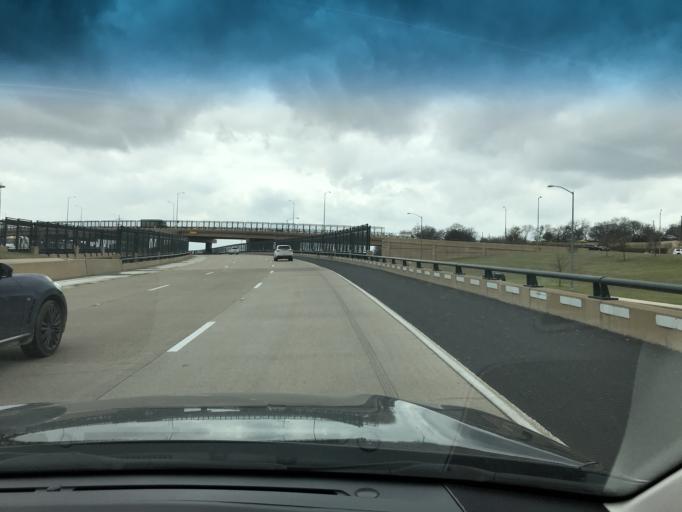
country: US
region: Texas
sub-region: Tarrant County
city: Westworth
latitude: 32.7212
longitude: -97.3849
